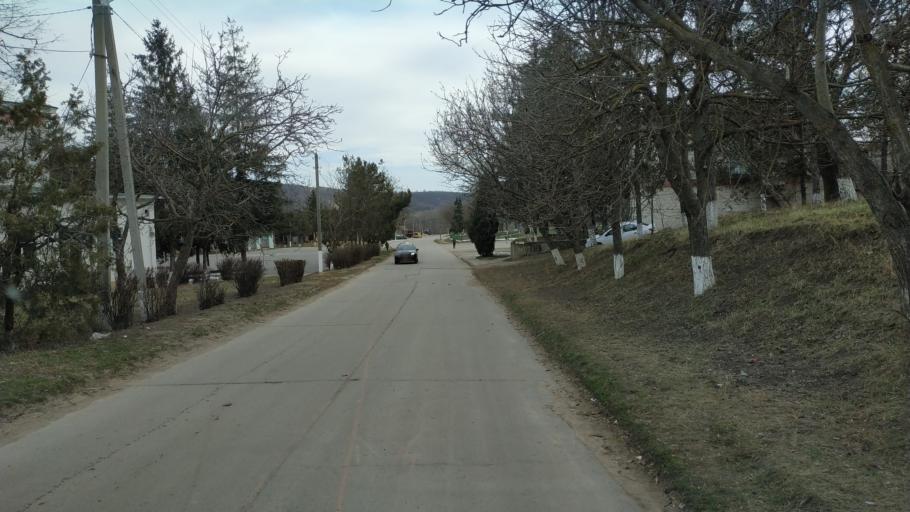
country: MD
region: Hincesti
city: Dancu
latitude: 46.9240
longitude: 28.2658
